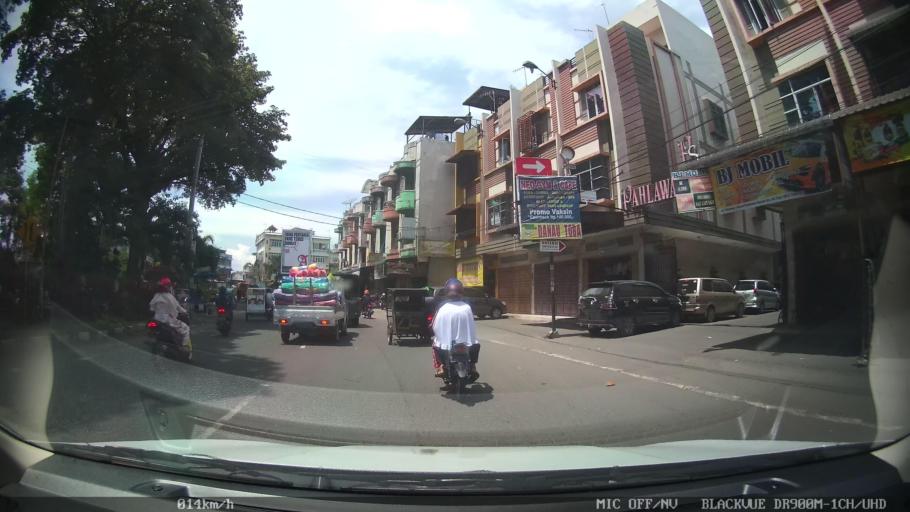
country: ID
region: North Sumatra
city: Binjai
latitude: 3.6099
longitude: 98.4930
